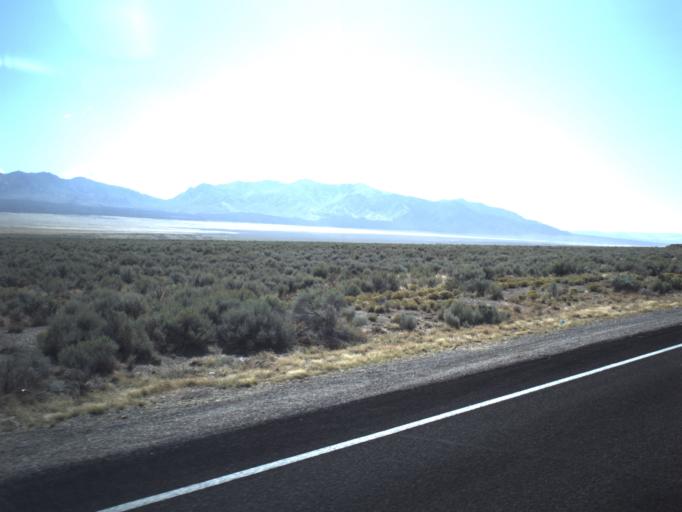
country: US
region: Utah
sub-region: Beaver County
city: Milford
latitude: 38.4416
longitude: -113.0098
